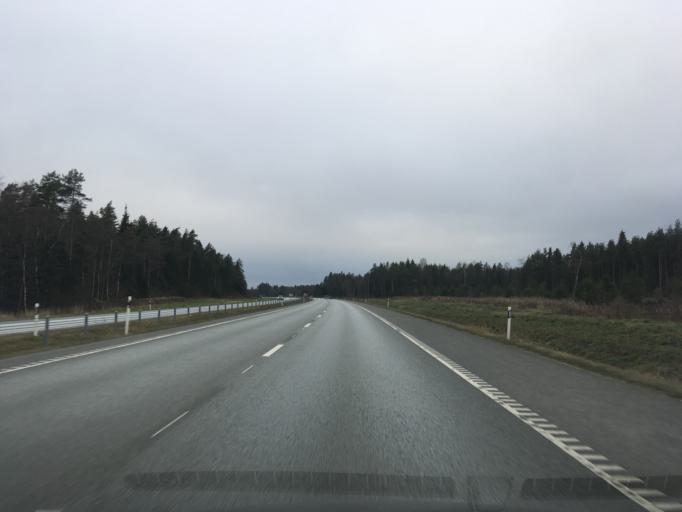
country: EE
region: Laeaene-Virumaa
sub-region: Kadrina vald
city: Kadrina
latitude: 59.4608
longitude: 26.0297
